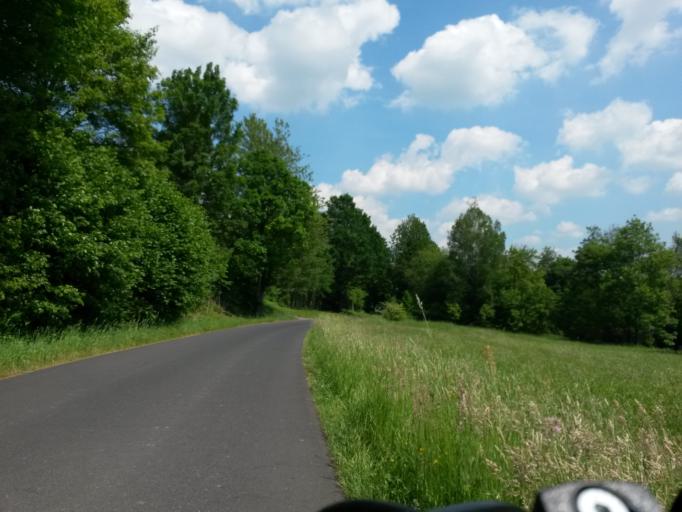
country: DE
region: Bavaria
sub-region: Regierungsbezirk Unterfranken
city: Euerdorf
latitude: 50.1622
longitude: 9.9972
